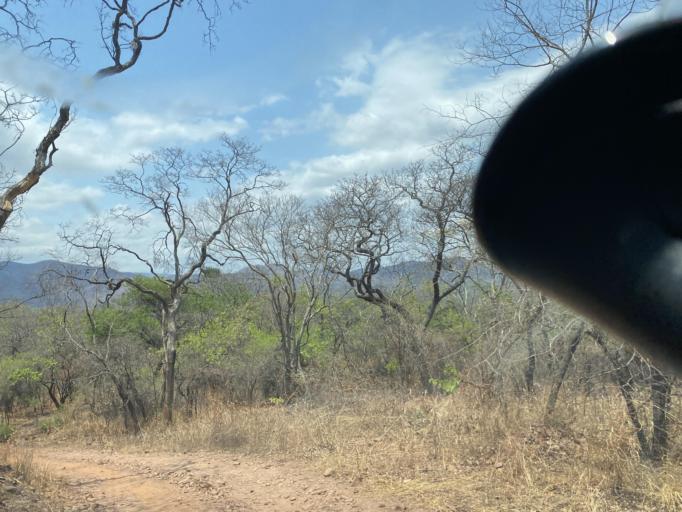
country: ZM
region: Lusaka
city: Luangwa
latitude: -15.1719
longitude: 29.7110
